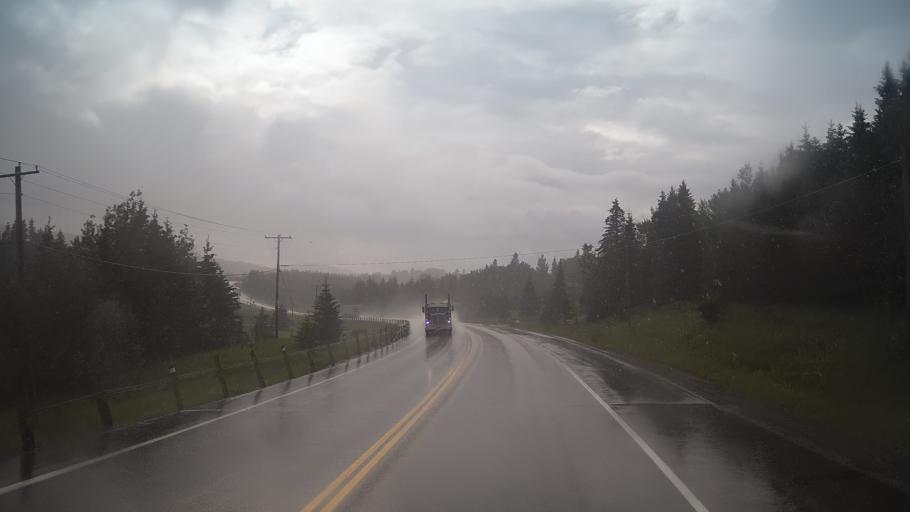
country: CA
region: Ontario
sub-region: Thunder Bay District
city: Thunder Bay
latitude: 48.5343
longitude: -89.6401
